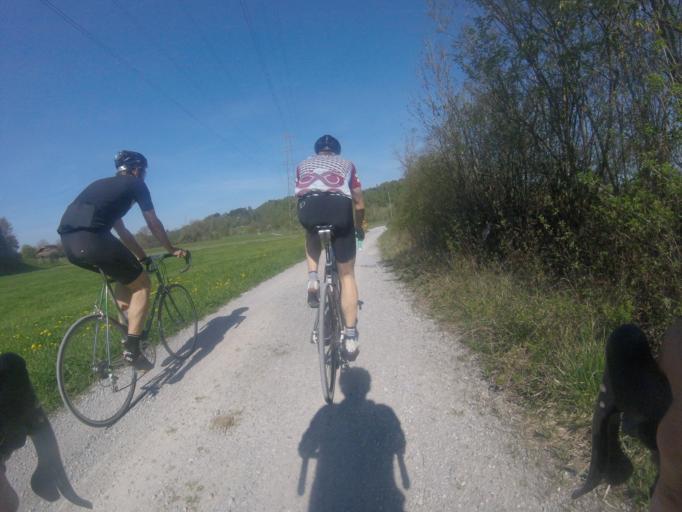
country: CH
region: Bern
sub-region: Bern-Mittelland District
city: Muhleberg
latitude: 46.9746
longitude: 7.2564
